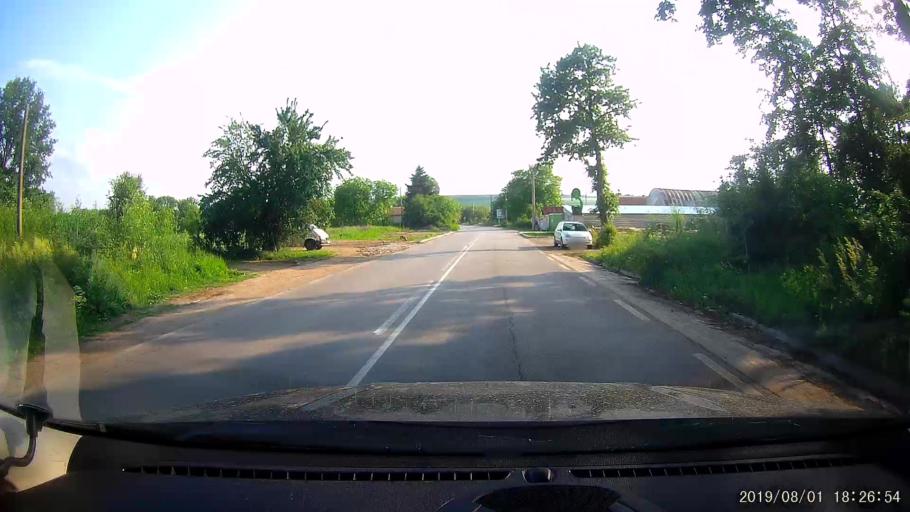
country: BG
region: Shumen
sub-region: Obshtina Venets
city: Venets
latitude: 43.5944
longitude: 26.9842
